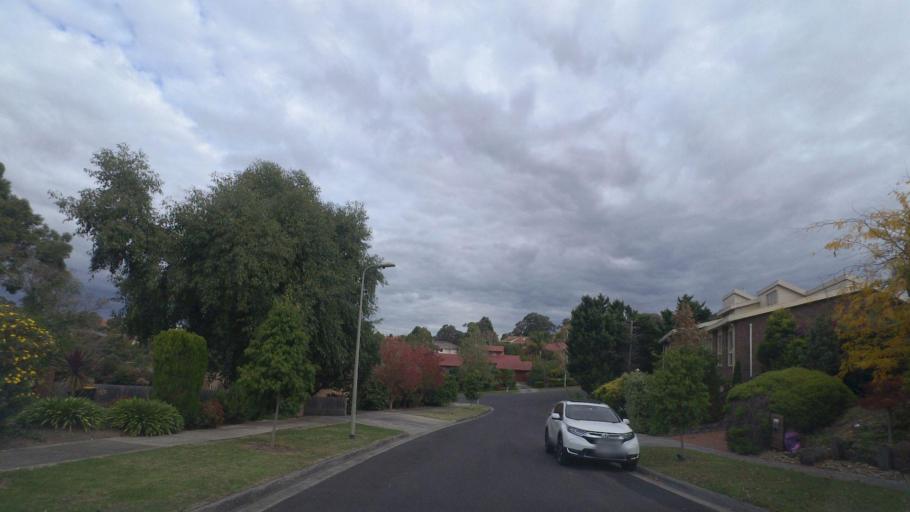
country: AU
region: Victoria
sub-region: Manningham
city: Donvale
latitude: -37.7562
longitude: 145.1771
